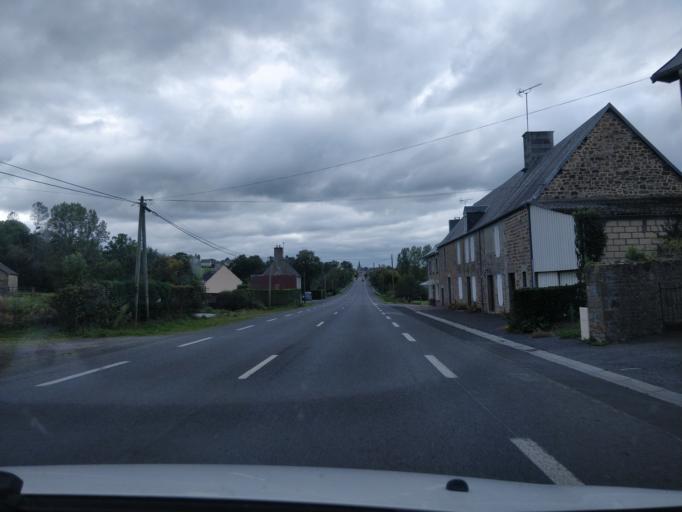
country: FR
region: Lower Normandy
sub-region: Departement de la Manche
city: Villedieu-les-Poeles
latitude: 48.8333
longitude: -1.1794
